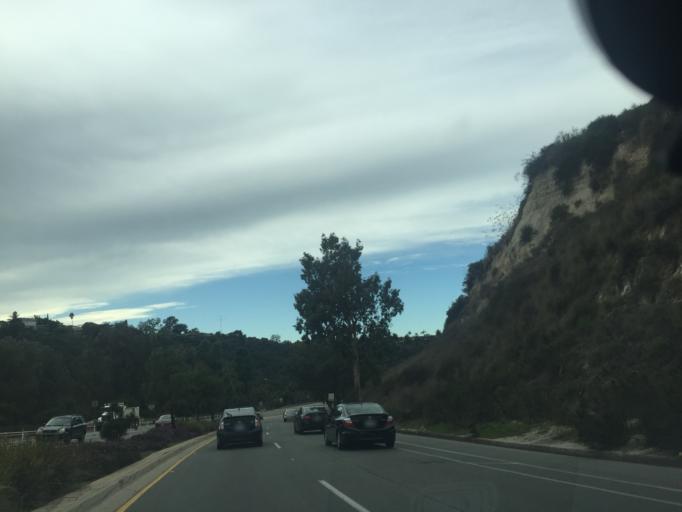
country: US
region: California
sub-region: San Diego County
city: Lemon Grove
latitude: 32.7700
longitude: -117.0863
